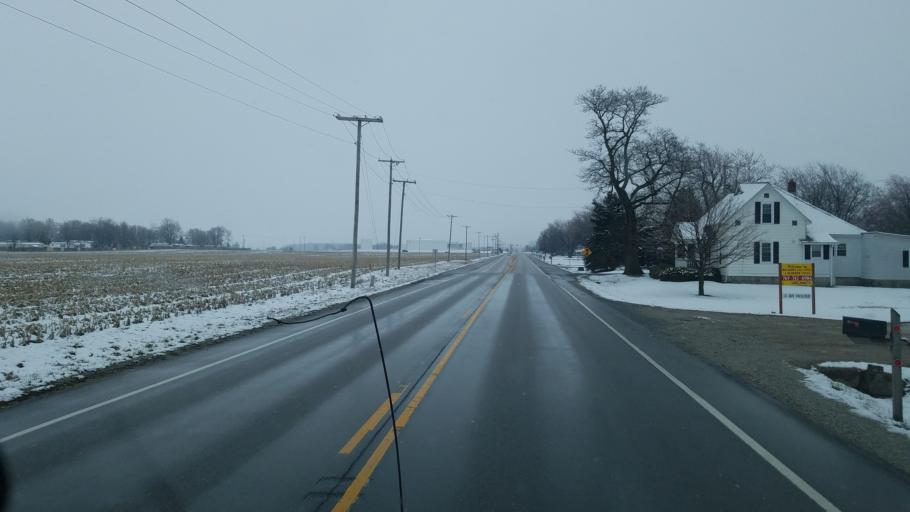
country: US
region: Indiana
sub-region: Delaware County
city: Eaton
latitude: 40.2770
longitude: -85.3746
